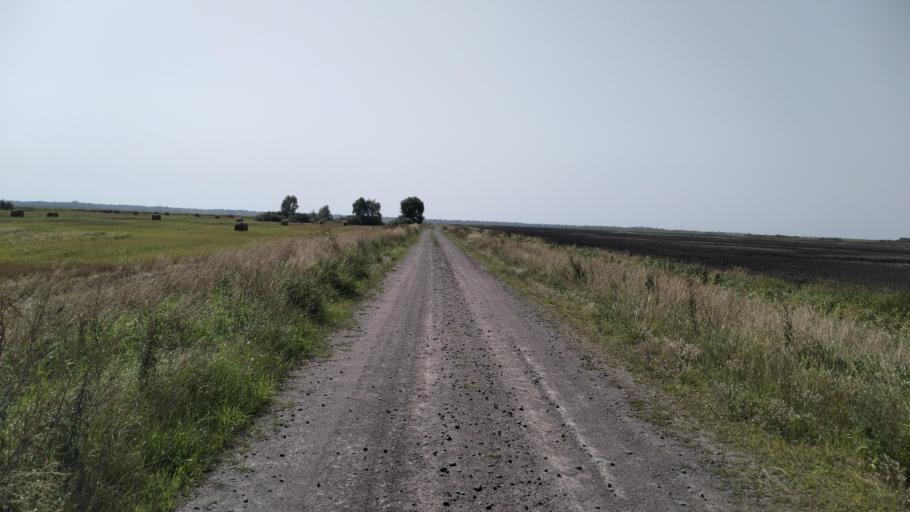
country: BY
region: Brest
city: Davyd-Haradok
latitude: 52.0003
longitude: 27.1653
